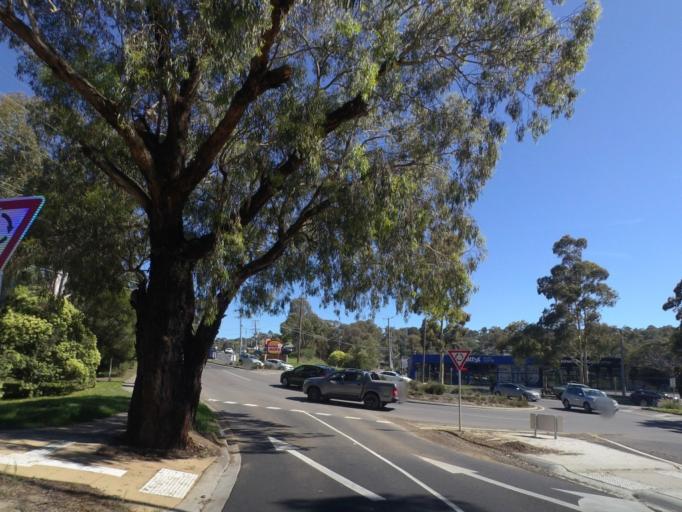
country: AU
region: Victoria
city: Saint Helena
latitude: -37.7184
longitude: 145.1377
